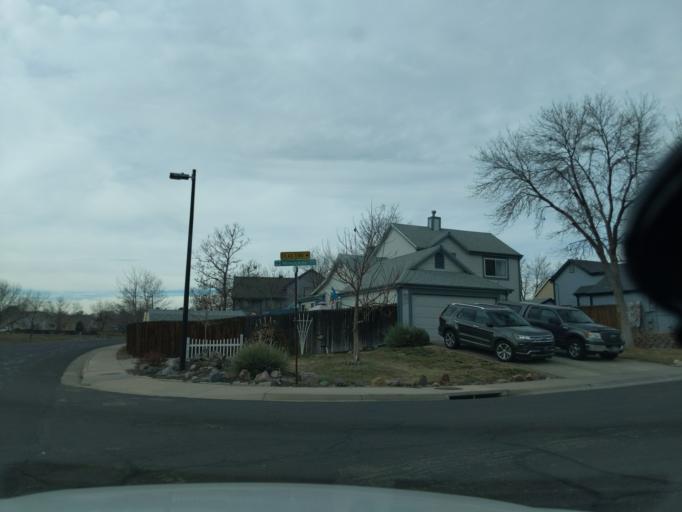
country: US
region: Colorado
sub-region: Adams County
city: Thornton
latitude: 39.8689
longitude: -104.9528
